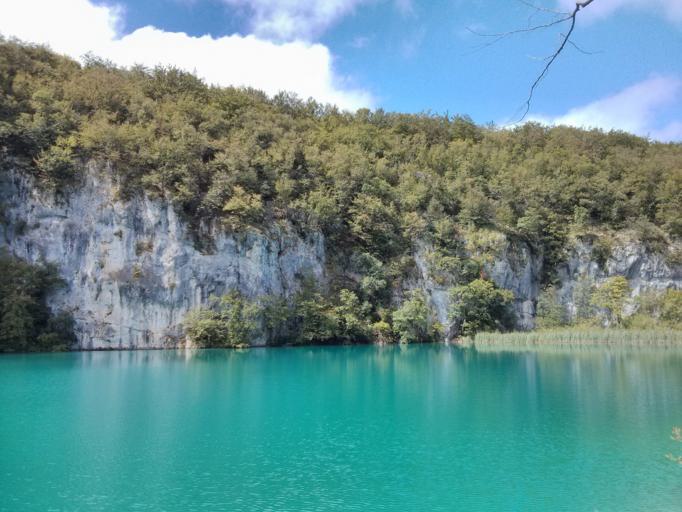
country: HR
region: Licko-Senjska
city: Jezerce
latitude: 44.8973
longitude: 15.6110
